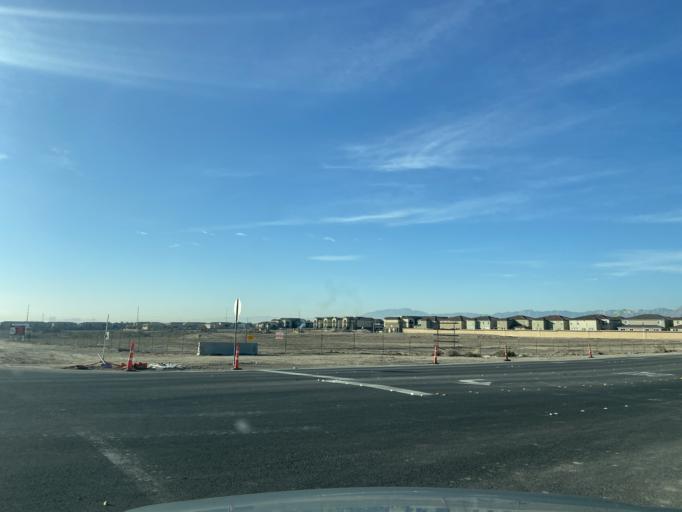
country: US
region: Nevada
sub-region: Clark County
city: Nellis Air Force Base
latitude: 36.2838
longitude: -115.1350
